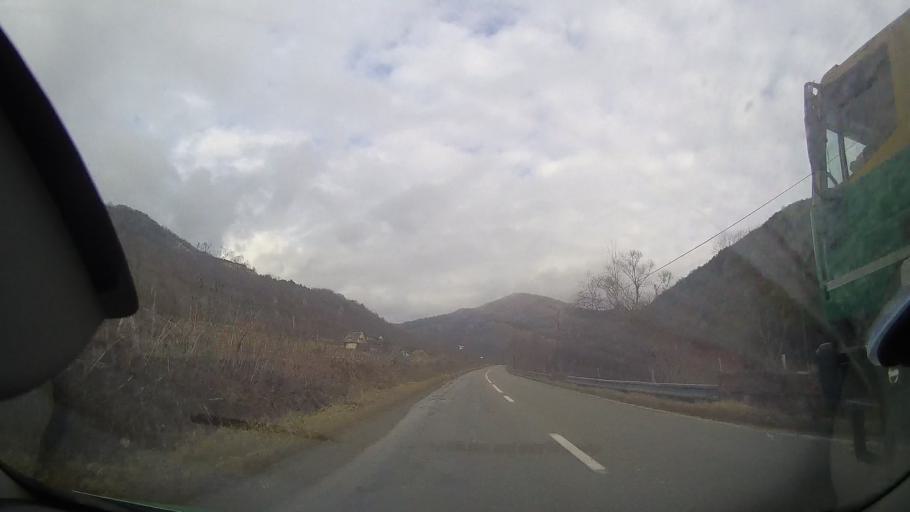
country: RO
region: Alba
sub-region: Comuna Ocolis
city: Ocolis
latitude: 46.4577
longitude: 23.4697
